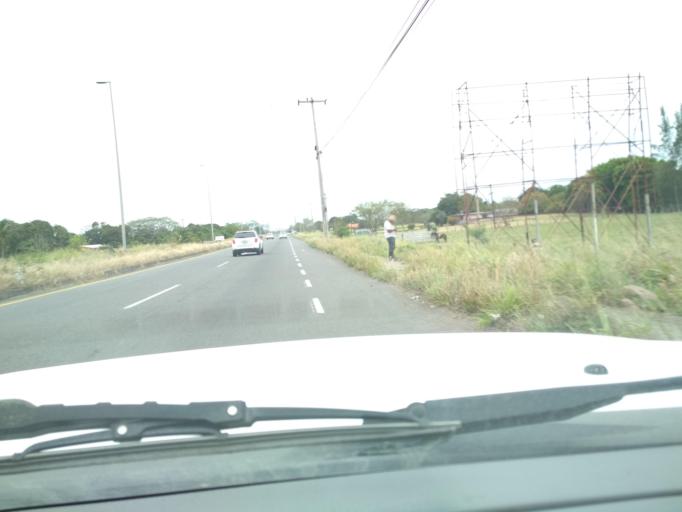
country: MX
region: Veracruz
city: Paso del Toro
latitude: 19.0595
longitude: -96.1321
